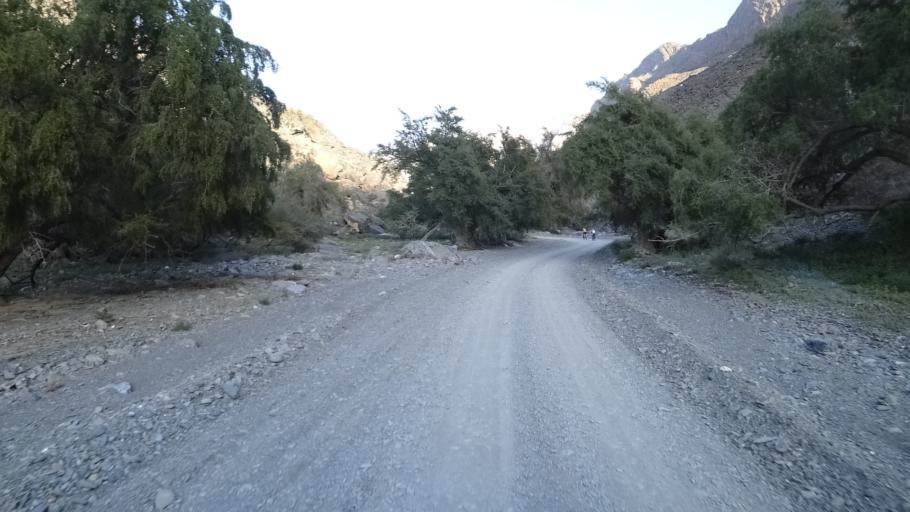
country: OM
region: Al Batinah
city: Bayt al `Awabi
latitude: 23.2546
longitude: 57.4043
